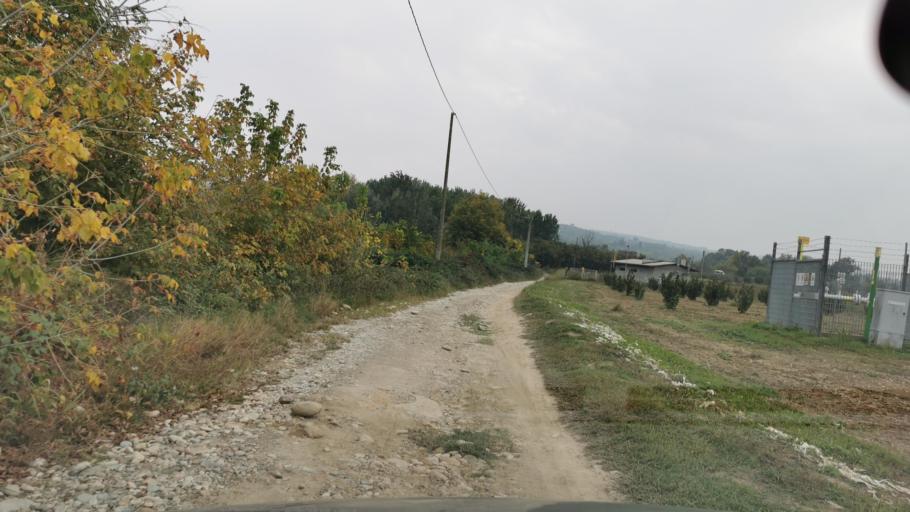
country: IT
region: Piedmont
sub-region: Provincia di Cuneo
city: Cinzano
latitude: 44.6891
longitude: 7.9130
